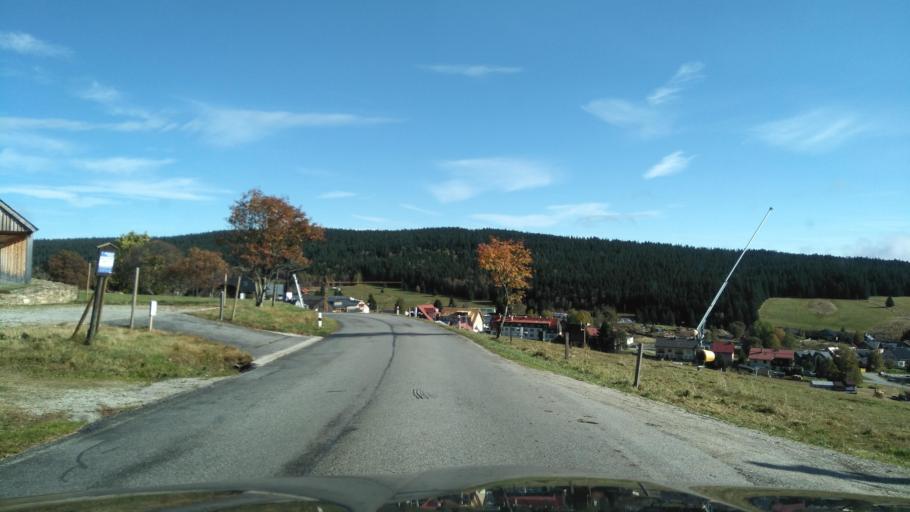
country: CZ
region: Jihocesky
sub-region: Okres Prachatice
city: Borova Lada
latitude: 49.0158
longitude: 13.5747
